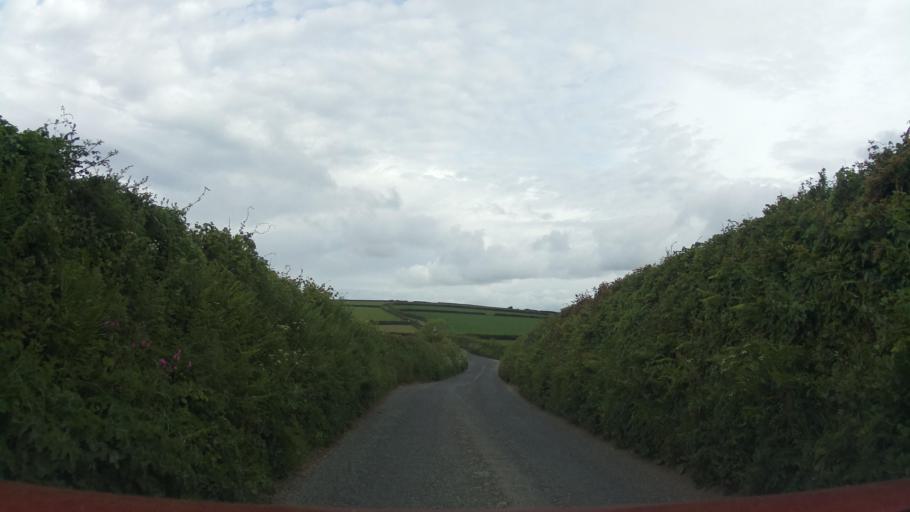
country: GB
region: England
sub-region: Devon
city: Dartmouth
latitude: 50.3215
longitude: -3.6371
